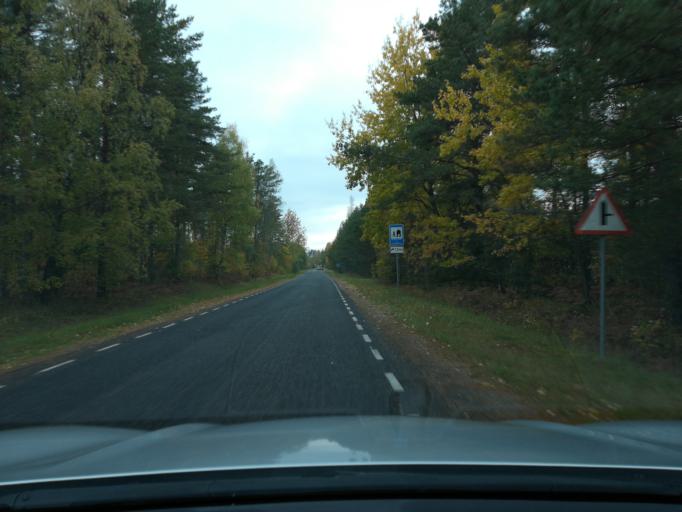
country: EE
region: Ida-Virumaa
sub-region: Johvi vald
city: Johvi
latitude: 59.0142
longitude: 27.4180
